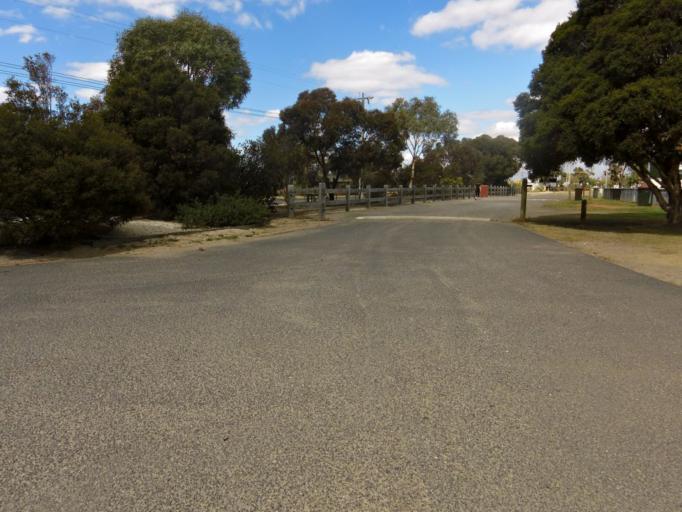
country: AU
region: Victoria
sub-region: Moorabool
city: Bacchus Marsh
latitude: -37.6574
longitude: 144.4422
